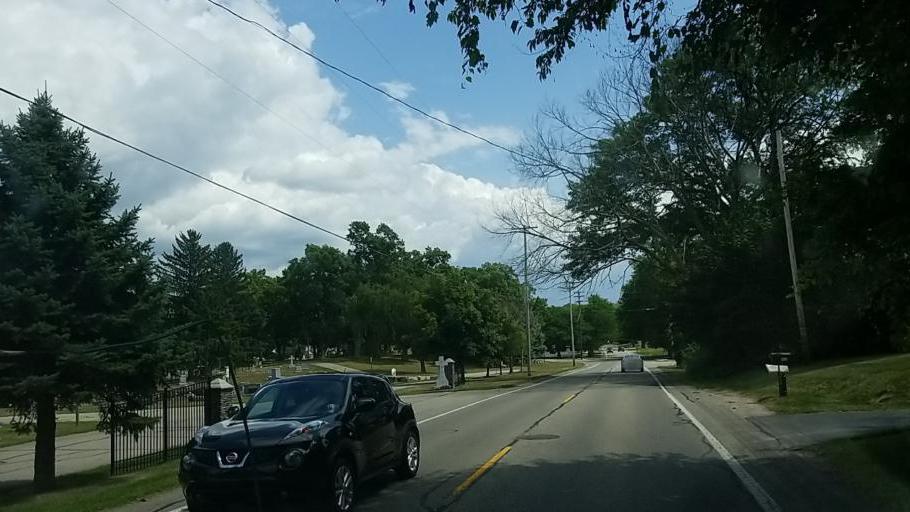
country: US
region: Michigan
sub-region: Kent County
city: Walker
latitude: 42.9940
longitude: -85.7170
